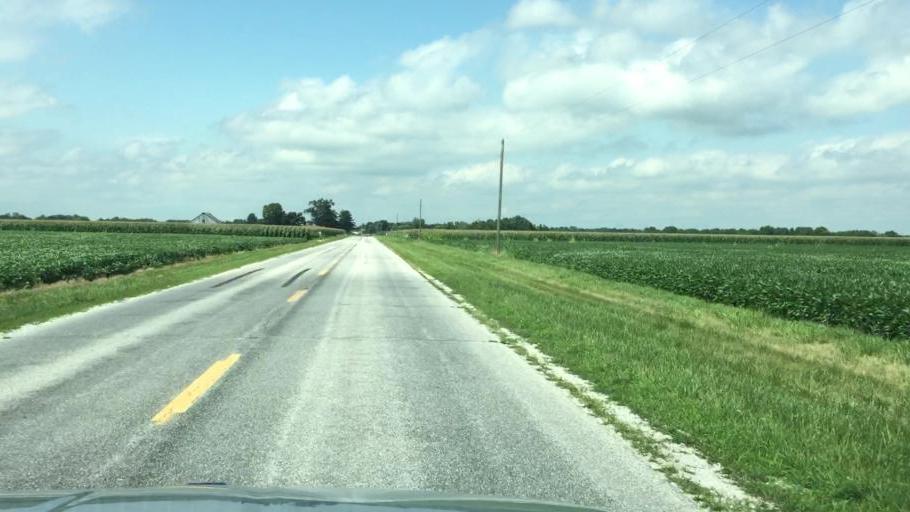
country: US
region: Illinois
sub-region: Hancock County
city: Nauvoo
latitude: 40.5131
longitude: -91.3082
